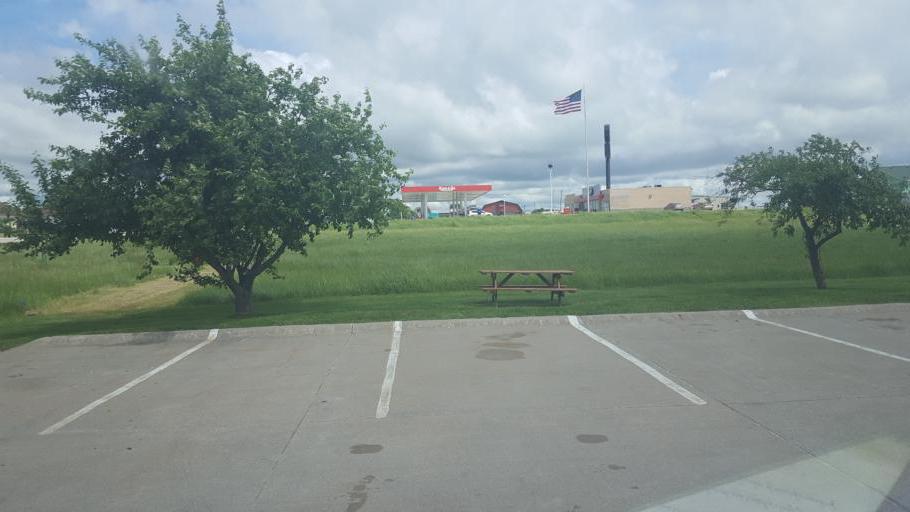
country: US
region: Iowa
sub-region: Decatur County
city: Lamoni
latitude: 40.6233
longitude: -93.8983
